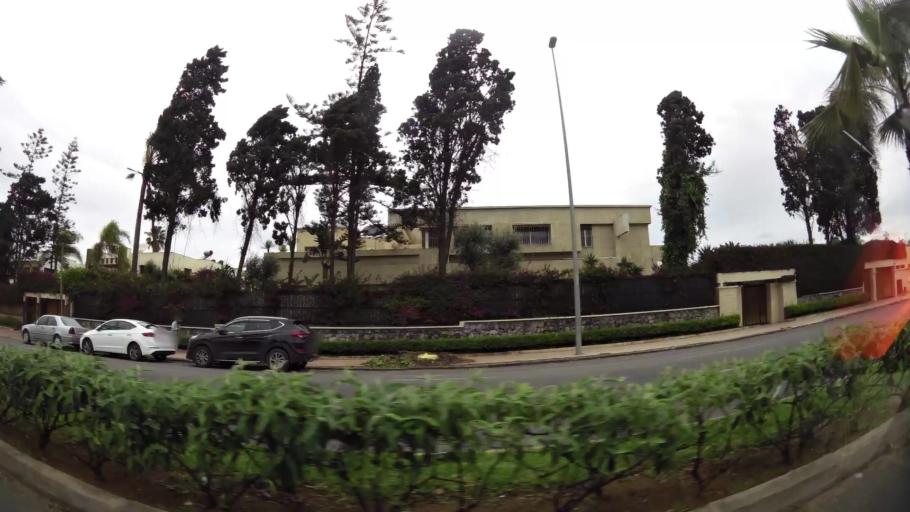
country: MA
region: Grand Casablanca
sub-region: Casablanca
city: Casablanca
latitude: 33.5620
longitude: -7.6167
